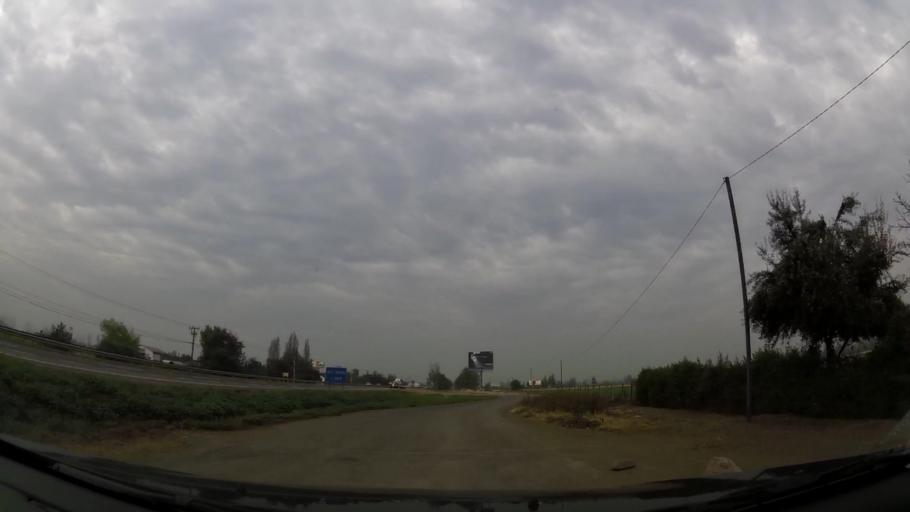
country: CL
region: Santiago Metropolitan
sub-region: Provincia de Chacabuco
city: Chicureo Abajo
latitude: -33.2278
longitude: -70.7626
